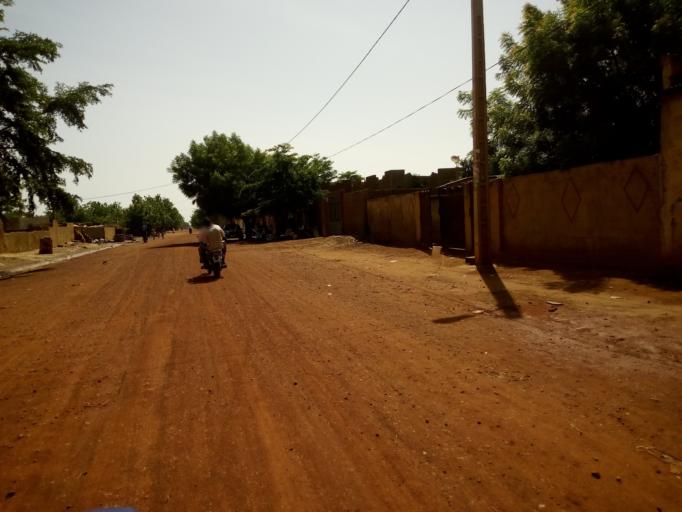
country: ML
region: Segou
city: Segou
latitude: 13.4242
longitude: -6.2155
